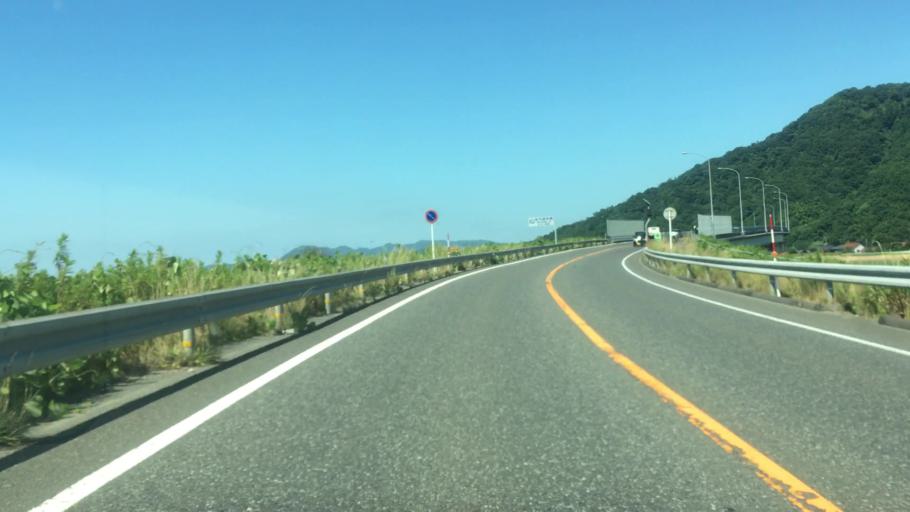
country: JP
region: Tottori
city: Tottori
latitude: 35.4373
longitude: 134.2057
